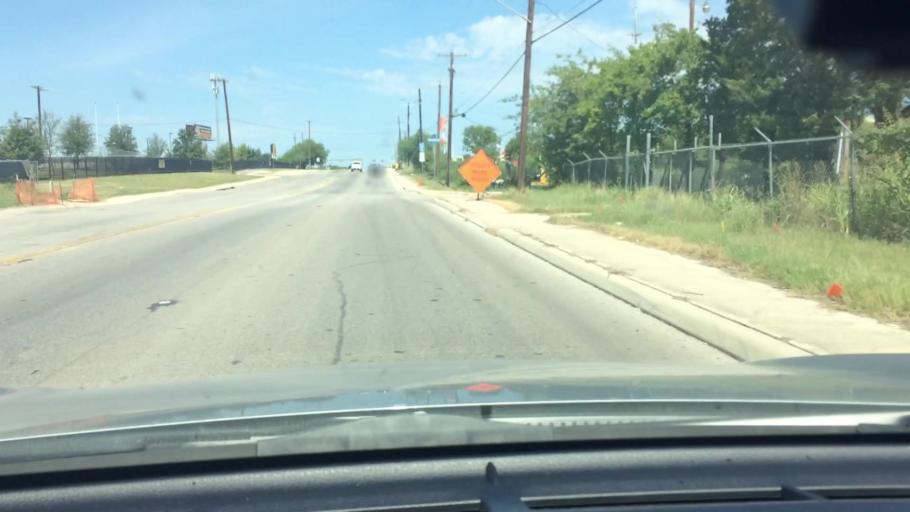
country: US
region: Texas
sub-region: Bexar County
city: San Antonio
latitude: 29.4008
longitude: -98.4406
